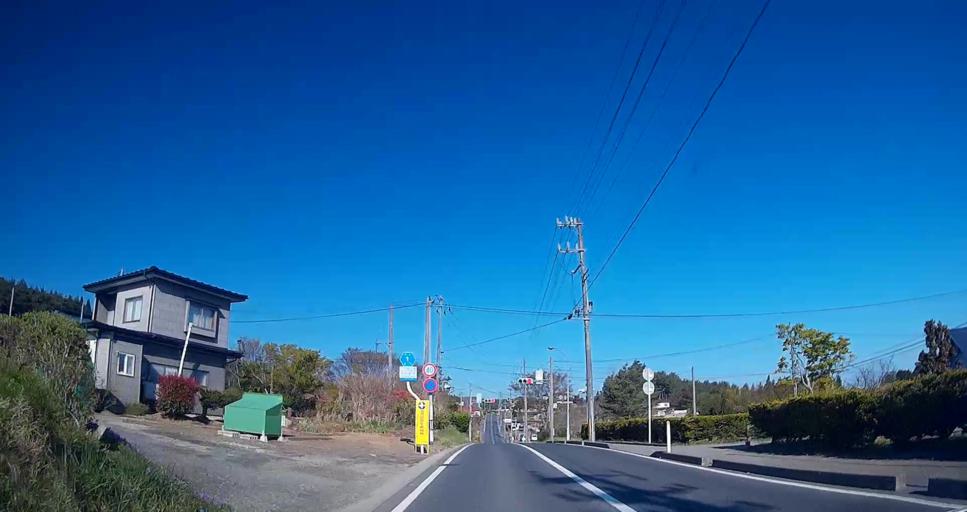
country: JP
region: Aomori
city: Hachinohe
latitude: 40.5151
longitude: 141.5932
